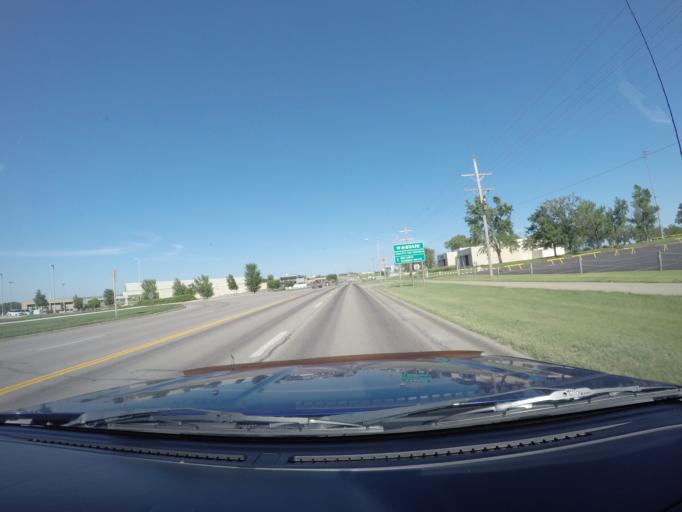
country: US
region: Kansas
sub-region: Riley County
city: Manhattan
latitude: 39.2040
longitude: -96.5911
